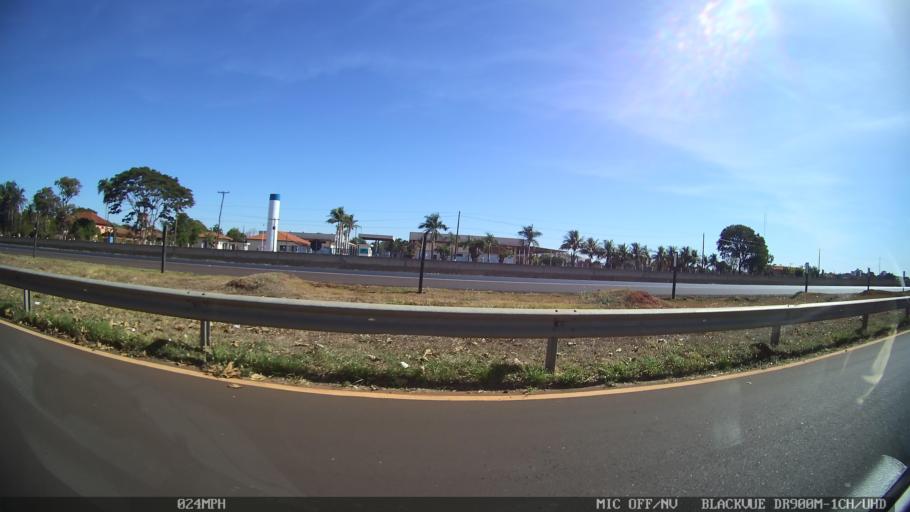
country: BR
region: Sao Paulo
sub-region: Barretos
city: Barretos
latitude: -20.5480
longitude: -48.5924
